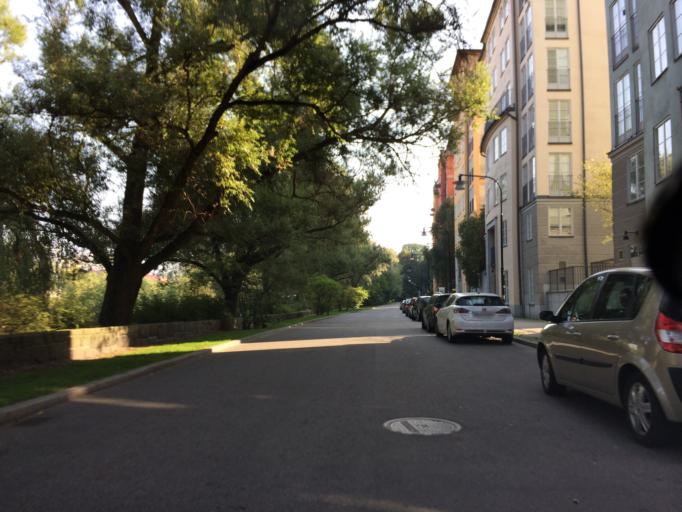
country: SE
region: Stockholm
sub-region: Stockholms Kommun
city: Stockholm
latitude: 59.3363
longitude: 18.0371
